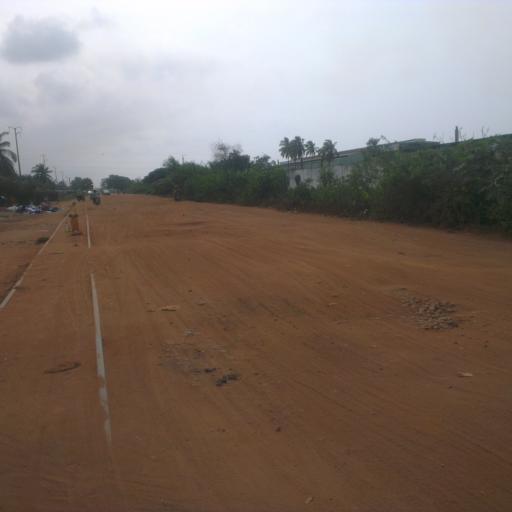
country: TG
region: Maritime
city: Lome
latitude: 6.1627
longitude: 1.2986
